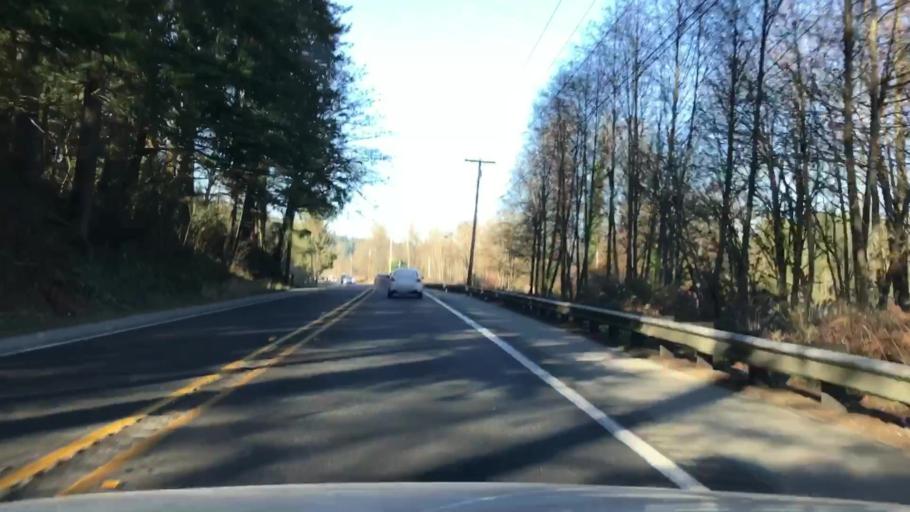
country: US
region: Washington
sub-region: King County
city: Maple Valley
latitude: 47.4319
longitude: -122.0579
